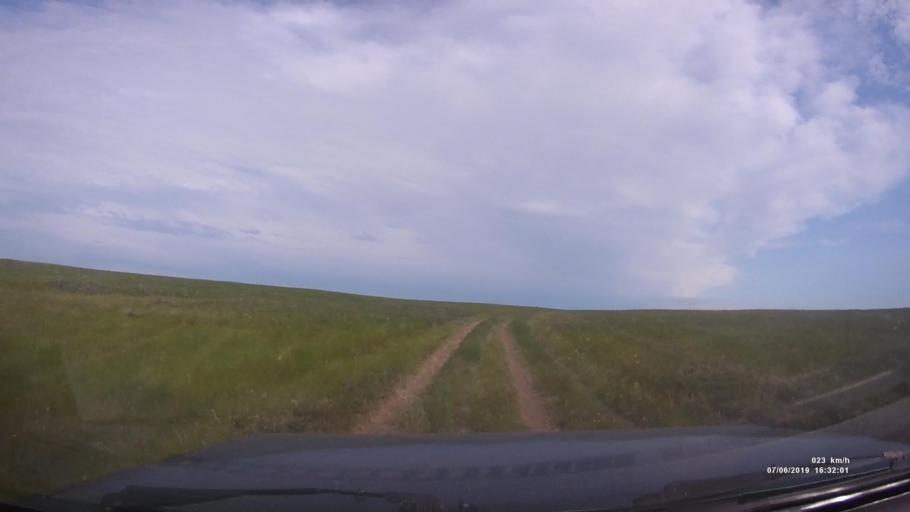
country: RU
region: Rostov
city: Staraya Stanitsa
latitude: 48.2547
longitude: 40.3286
